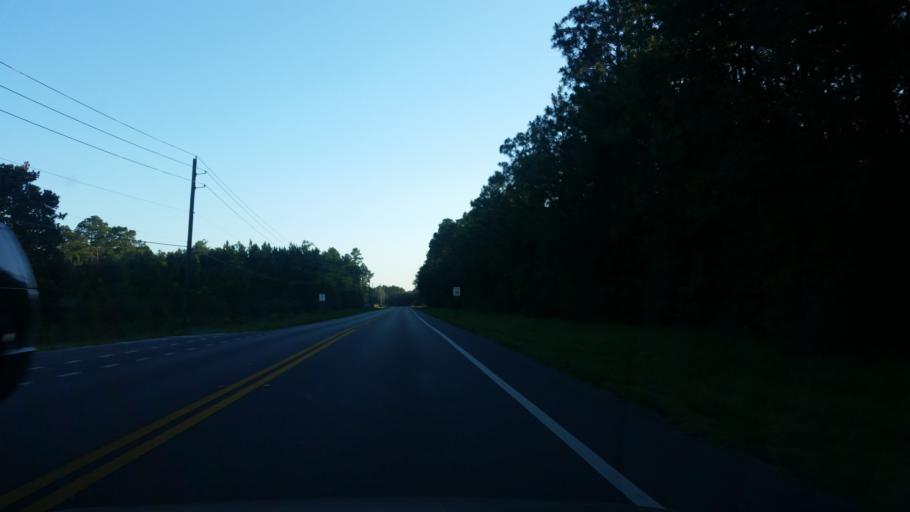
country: US
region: Florida
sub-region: Escambia County
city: Cantonment
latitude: 30.5928
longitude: -87.3281
